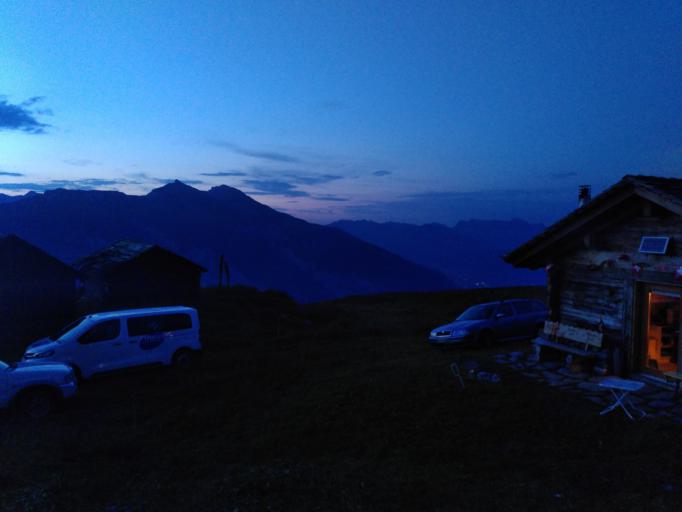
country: CH
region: Grisons
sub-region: Imboden District
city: Domat
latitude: 46.8004
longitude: 9.4582
